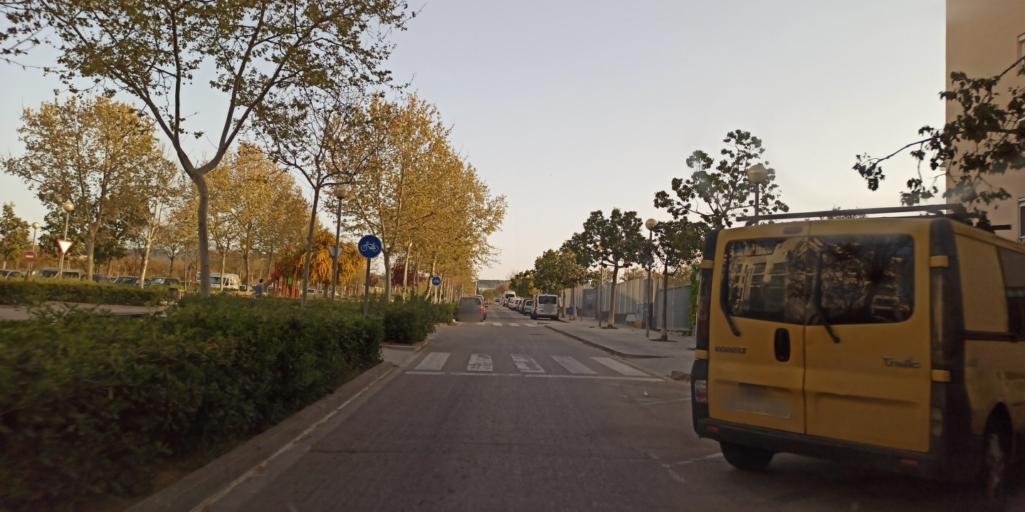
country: ES
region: Catalonia
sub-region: Provincia de Barcelona
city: Vilanova i la Geltru
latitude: 41.2317
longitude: 1.7261
